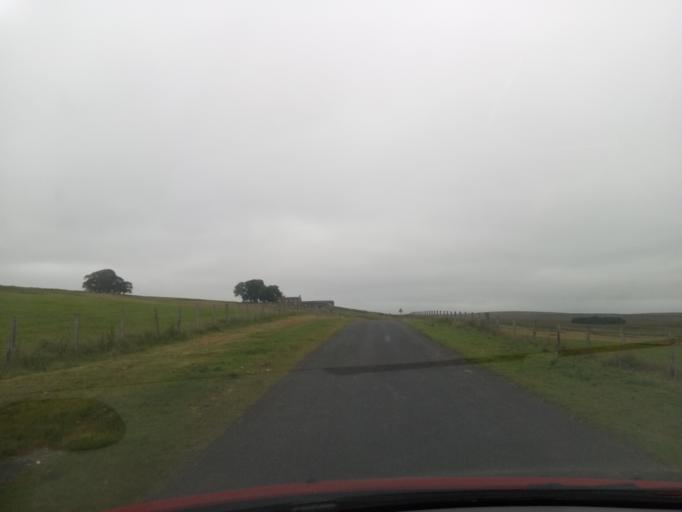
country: GB
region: England
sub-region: Northumberland
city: Rochester
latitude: 55.2917
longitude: -2.2069
